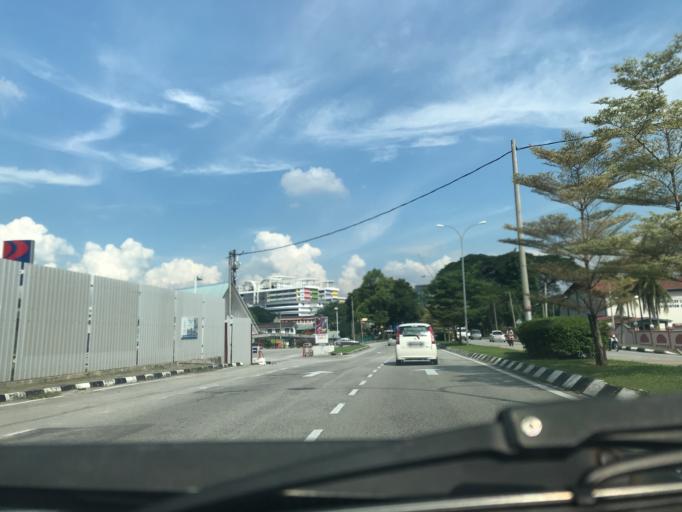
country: MY
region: Perak
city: Ipoh
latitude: 4.6072
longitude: 101.0847
